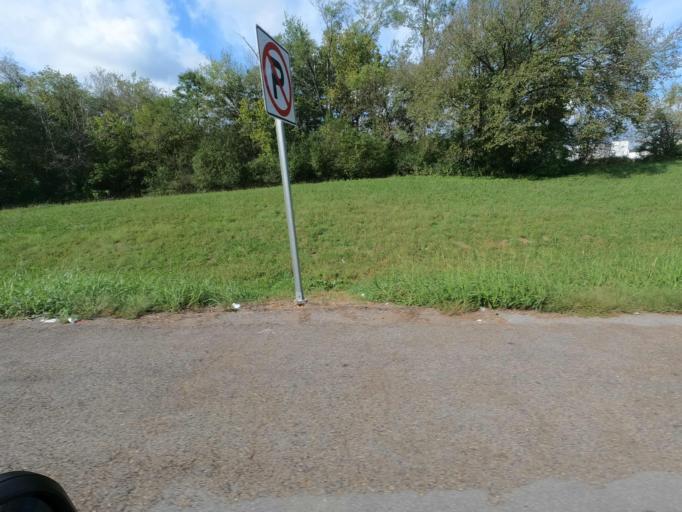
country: US
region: Tennessee
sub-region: Loudon County
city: Loudon
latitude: 35.7858
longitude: -84.3439
